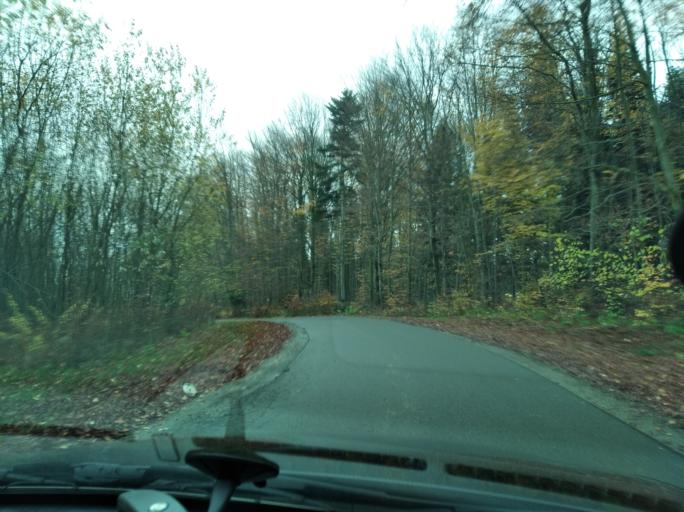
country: PL
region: Subcarpathian Voivodeship
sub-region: Powiat strzyzowski
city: Strzyzow
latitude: 49.9083
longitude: 21.7786
